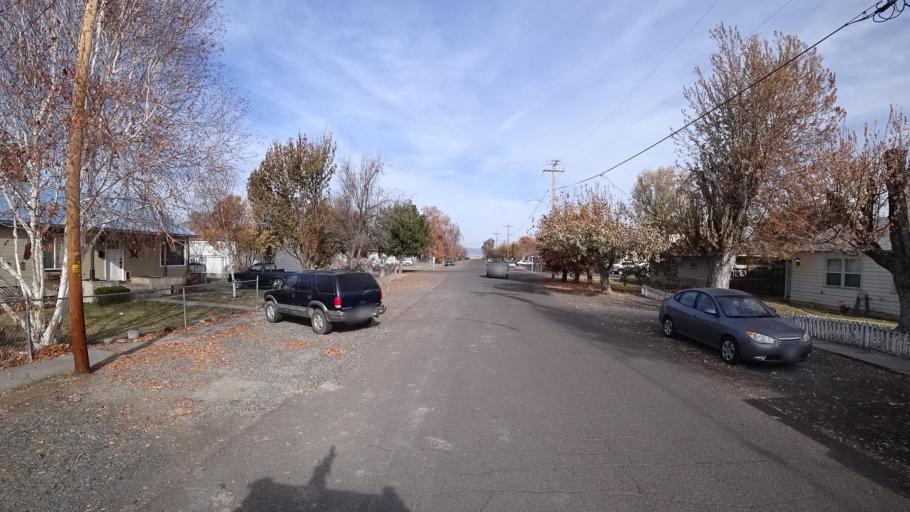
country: US
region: California
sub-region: Siskiyou County
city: Tulelake
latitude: 41.9581
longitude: -121.4792
